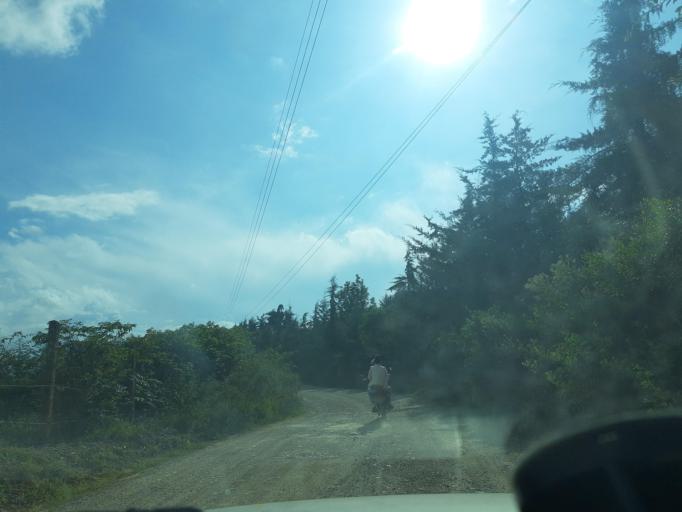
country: CO
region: Boyaca
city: Villa de Leiva
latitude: 5.6539
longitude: -73.5359
